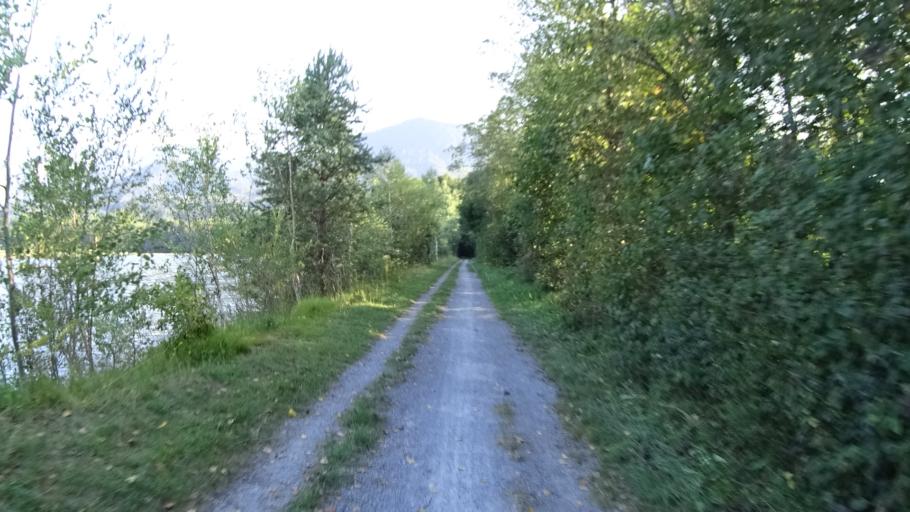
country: AT
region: Carinthia
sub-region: Politischer Bezirk Villach Land
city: Sankt Jakob
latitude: 46.5390
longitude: 14.0884
